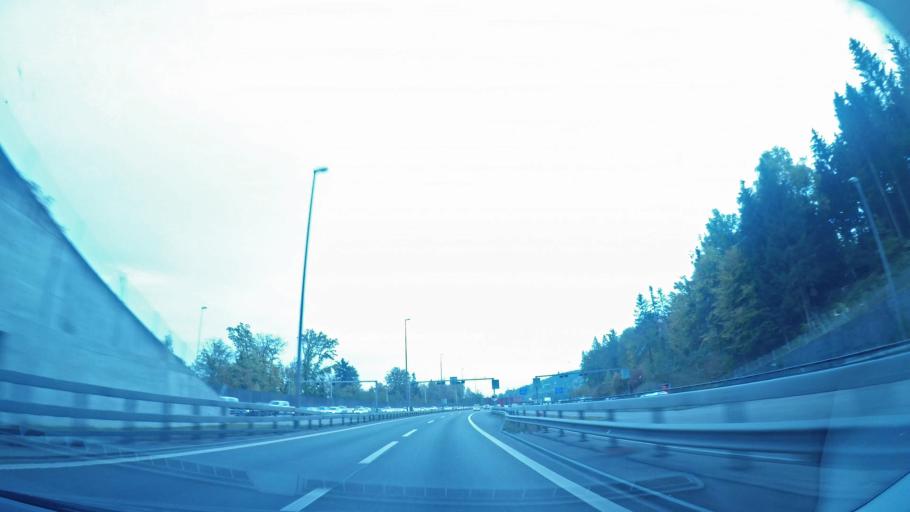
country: CH
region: Aargau
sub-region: Bezirk Baden
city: Baden
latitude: 47.4587
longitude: 8.2914
